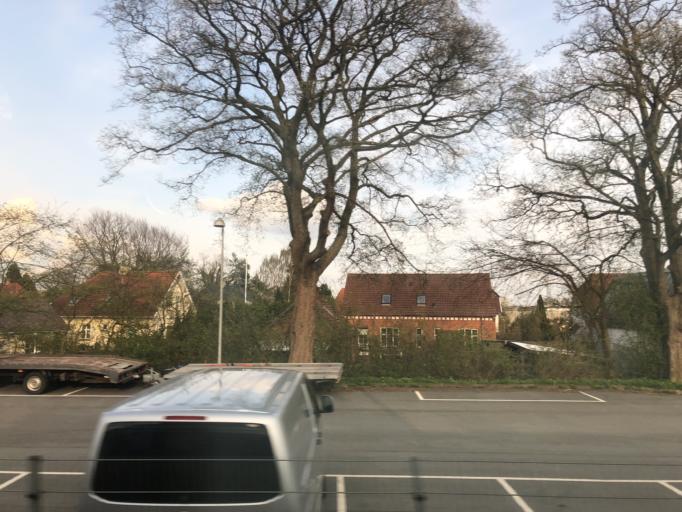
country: DK
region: Zealand
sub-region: Koge Kommune
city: Borup
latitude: 55.4920
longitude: 11.9715
